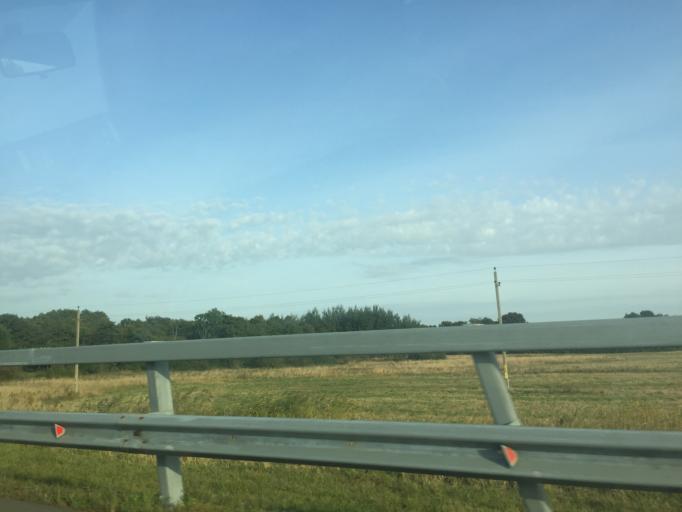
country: RU
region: Kaliningrad
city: Gur'yevsk
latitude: 54.8697
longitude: 20.5691
